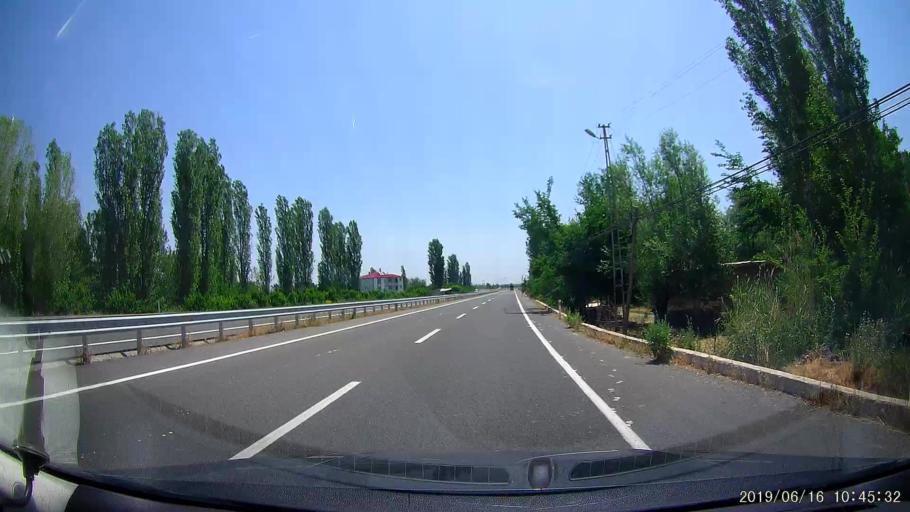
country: AM
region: Armavir
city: Shenavan
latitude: 40.0273
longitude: 43.8702
